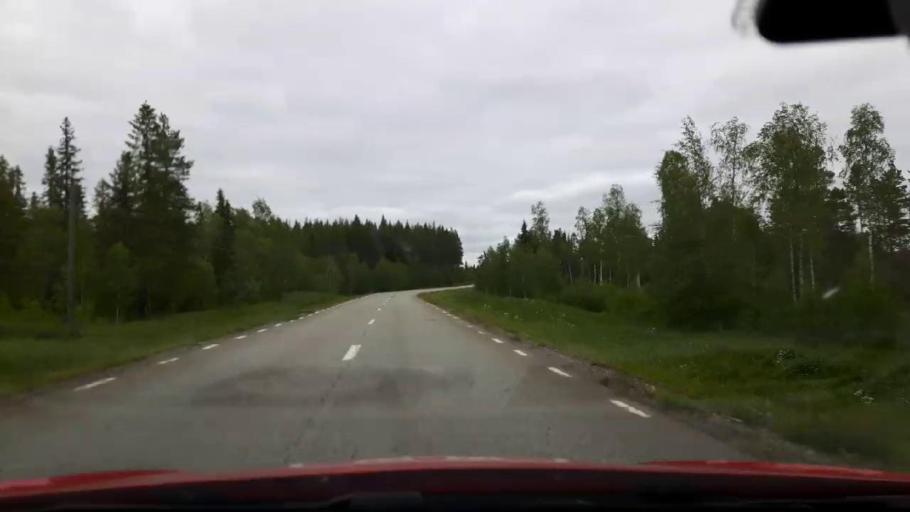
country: SE
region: Jaemtland
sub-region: Stroemsunds Kommun
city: Stroemsund
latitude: 63.3829
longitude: 15.6837
